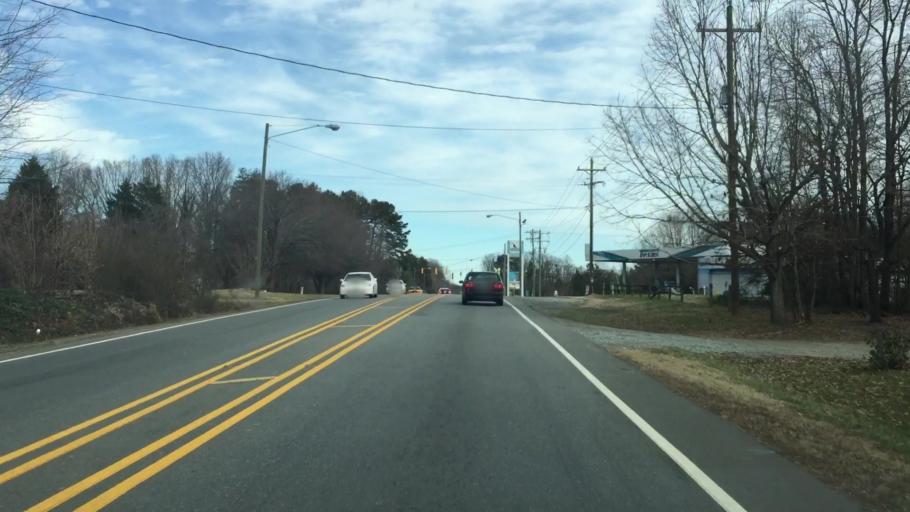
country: US
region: North Carolina
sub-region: Forsyth County
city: Walkertown
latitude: 36.1548
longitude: -80.1476
